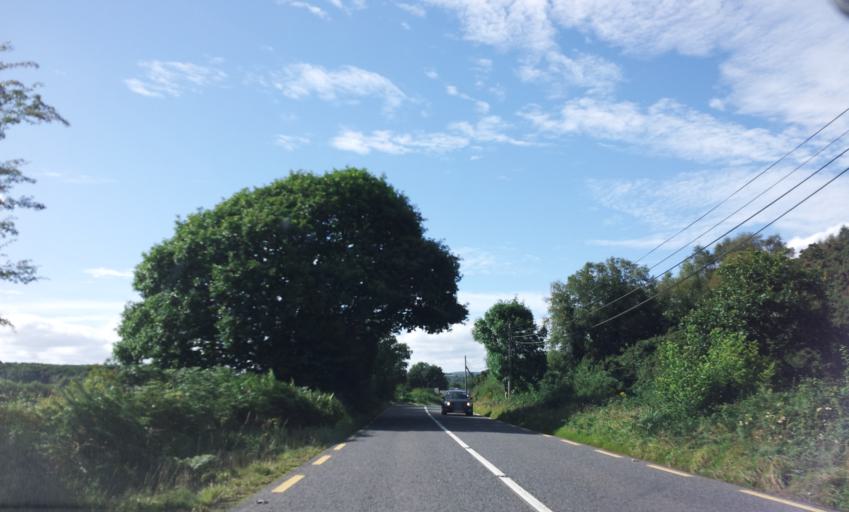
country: IE
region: Munster
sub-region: County Cork
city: Macroom
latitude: 51.9109
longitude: -9.0485
